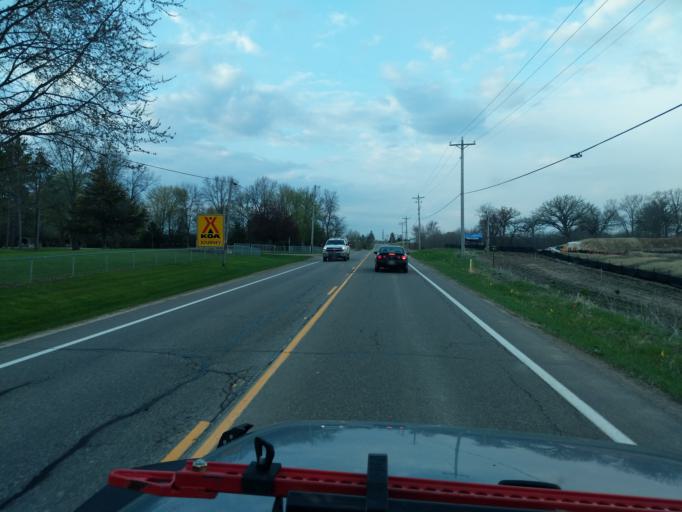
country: US
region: Minnesota
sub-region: Hennepin County
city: Rogers
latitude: 45.1450
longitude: -93.5221
